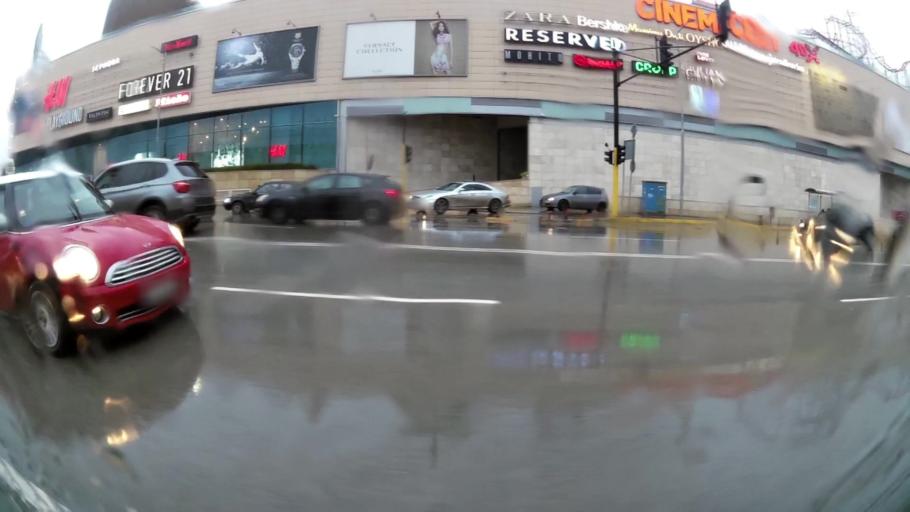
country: BG
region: Sofia-Capital
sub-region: Stolichna Obshtina
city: Sofia
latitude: 42.6578
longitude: 23.3162
